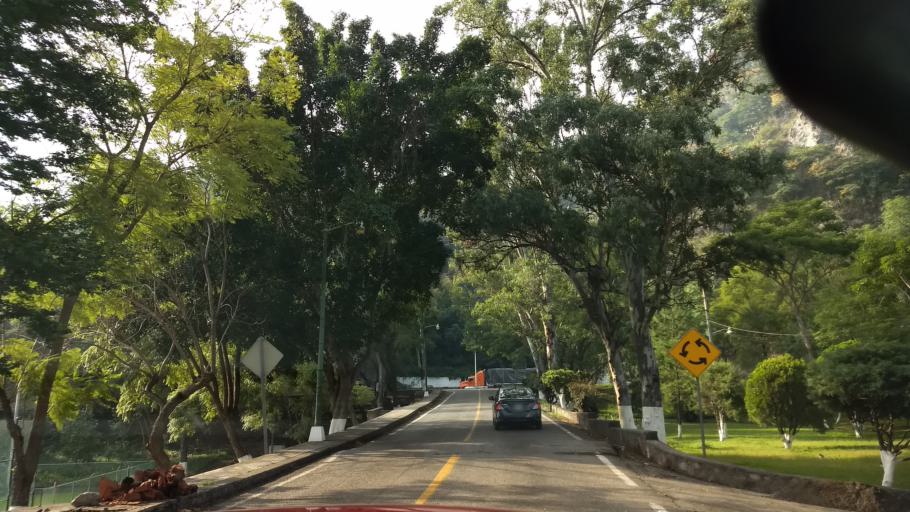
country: MX
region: Jalisco
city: Tuxpan
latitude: 19.5291
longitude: -103.4400
